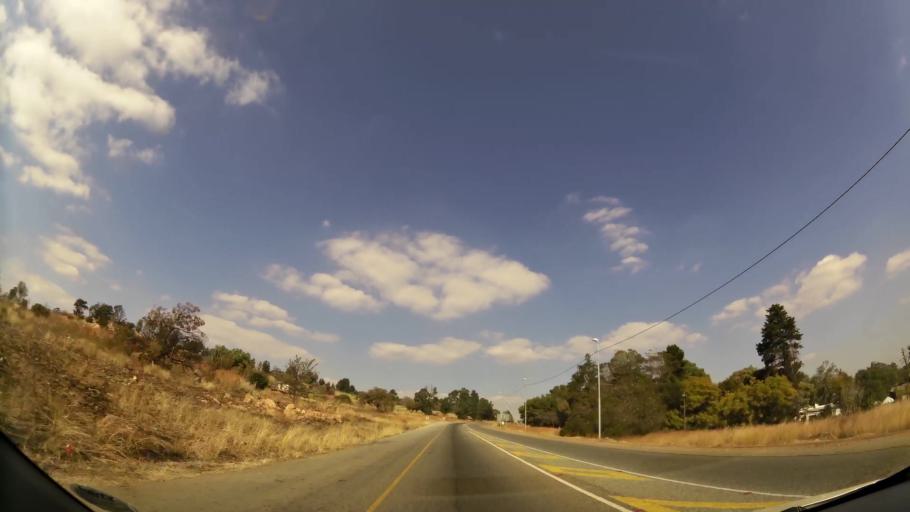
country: ZA
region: Gauteng
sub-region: West Rand District Municipality
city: Krugersdorp
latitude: -26.0371
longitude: 27.7406
